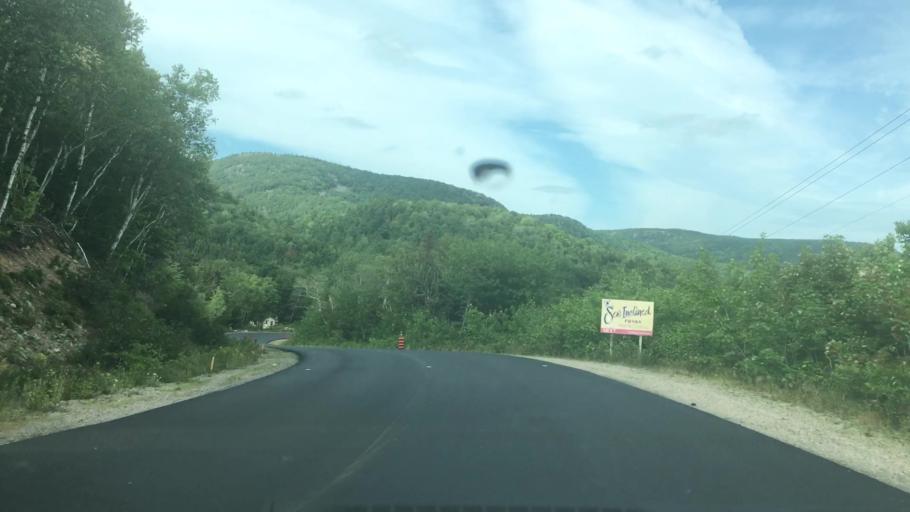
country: CA
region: Nova Scotia
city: Sydney Mines
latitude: 46.5429
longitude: -60.4144
